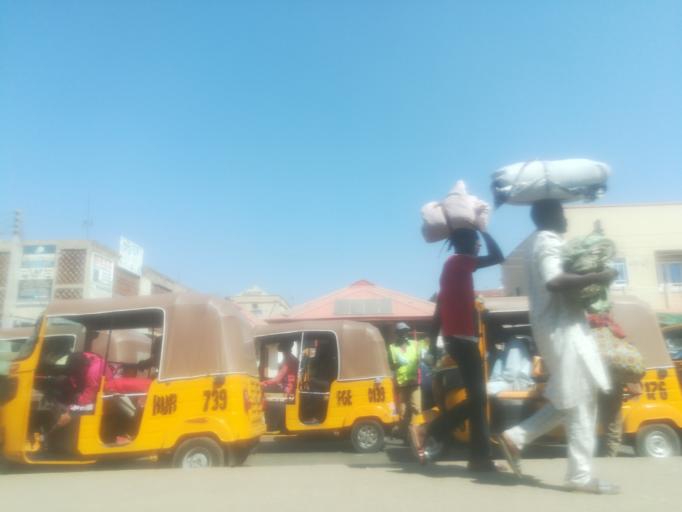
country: NG
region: Kano
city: Kano
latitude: 12.0144
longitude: 8.5401
